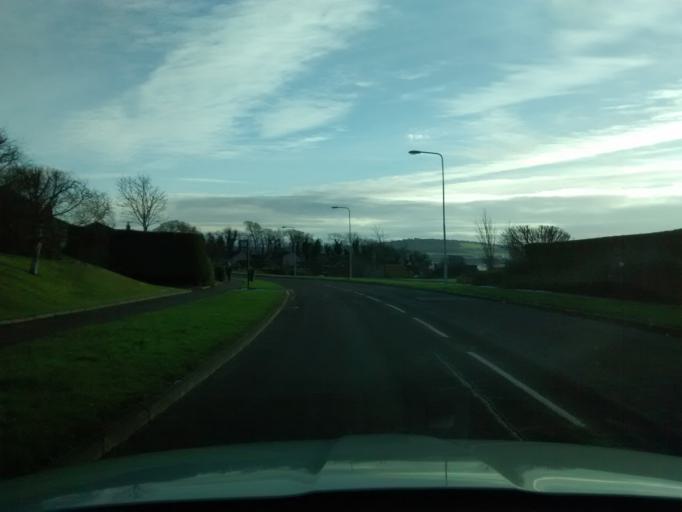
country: GB
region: Scotland
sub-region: Fife
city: Inverkeithing
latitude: 56.0307
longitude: -3.3647
